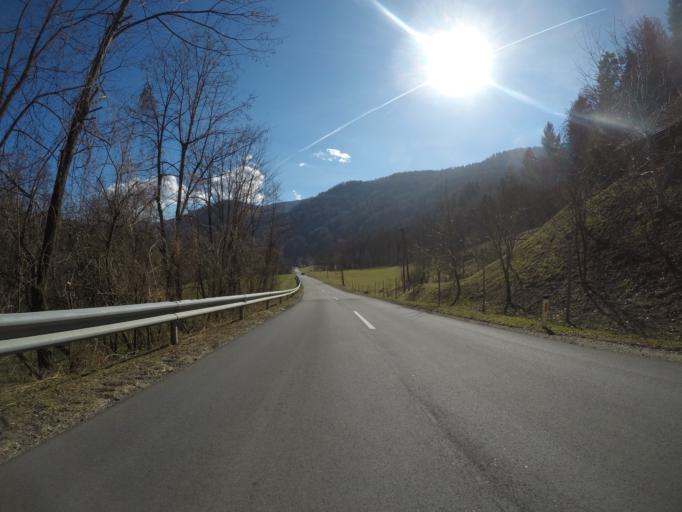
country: SI
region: Selnica ob Dravi
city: Selnica ob Dravi
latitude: 46.5395
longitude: 15.4522
